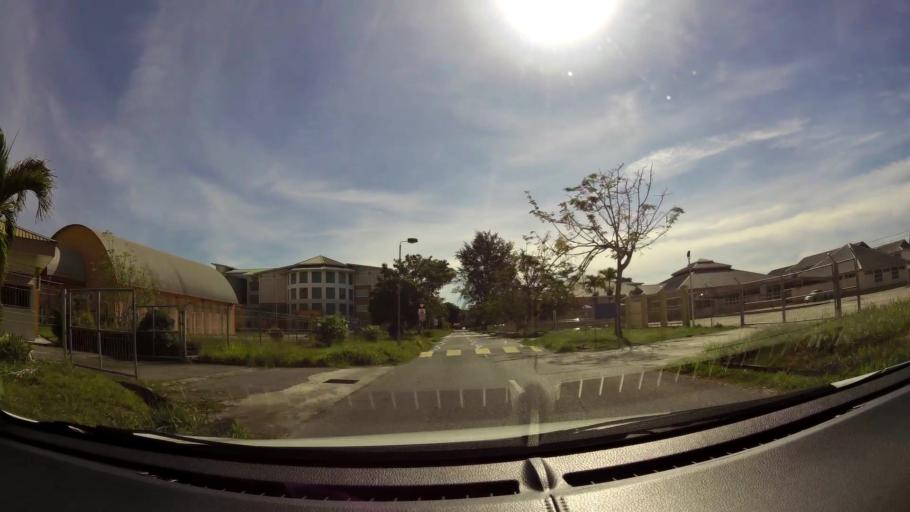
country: BN
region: Belait
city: Kuala Belait
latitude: 4.5803
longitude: 114.2063
